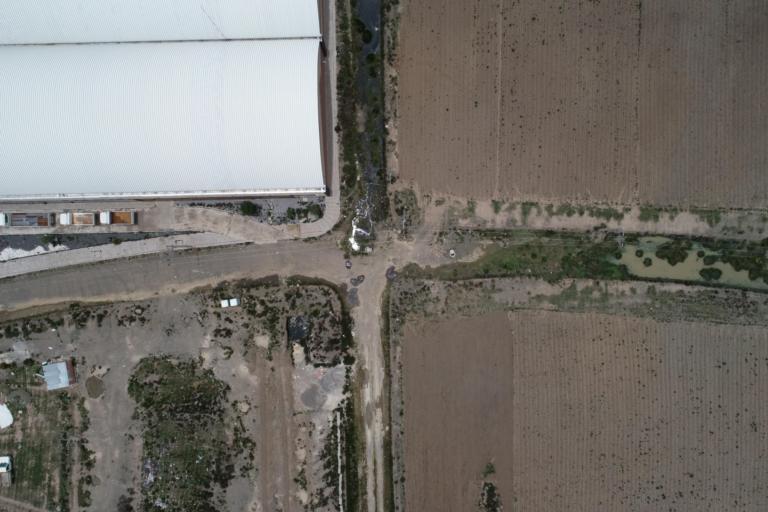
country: BO
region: La Paz
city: La Paz
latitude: -16.5183
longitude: -68.3002
